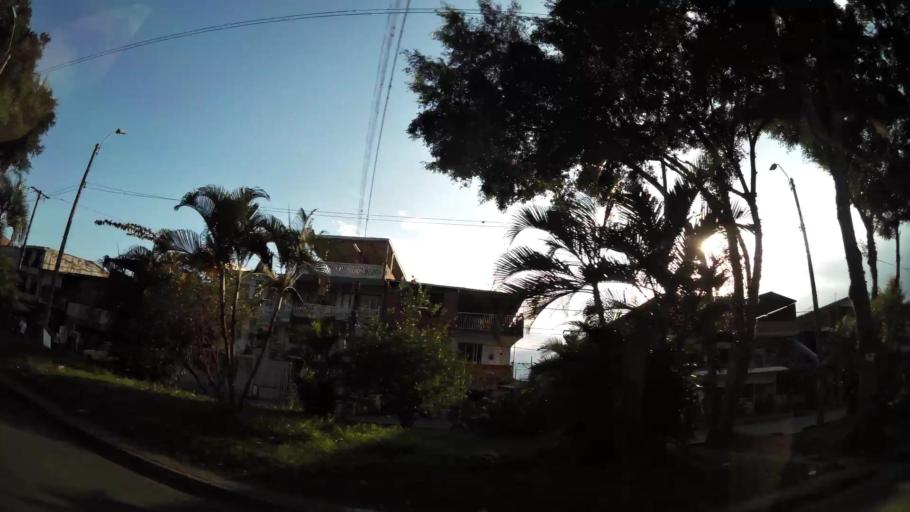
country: CO
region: Valle del Cauca
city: Cali
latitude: 3.4074
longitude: -76.5034
